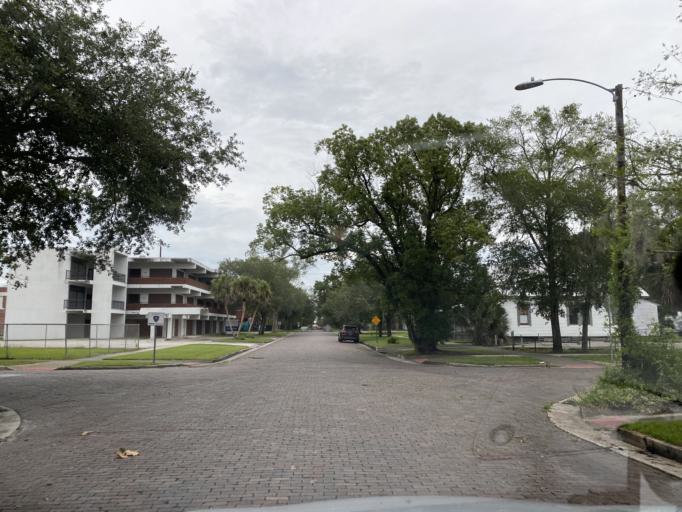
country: US
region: Florida
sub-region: Seminole County
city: Sanford
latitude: 28.8070
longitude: -81.2669
